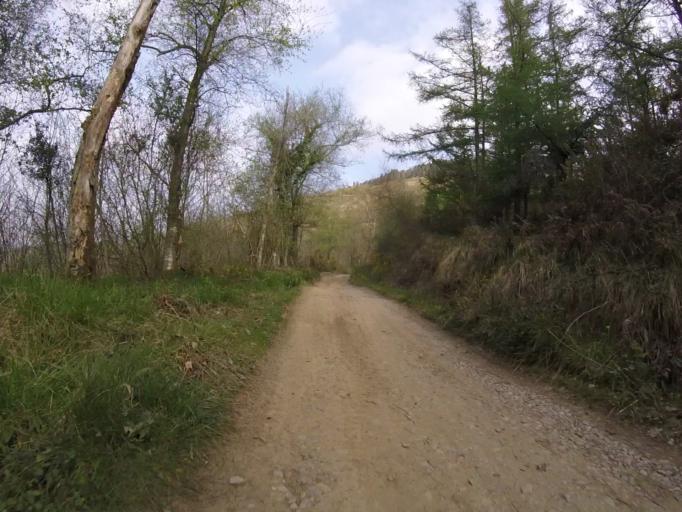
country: ES
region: Basque Country
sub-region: Provincia de Guipuzcoa
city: Usurbil
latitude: 43.2421
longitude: -2.0774
